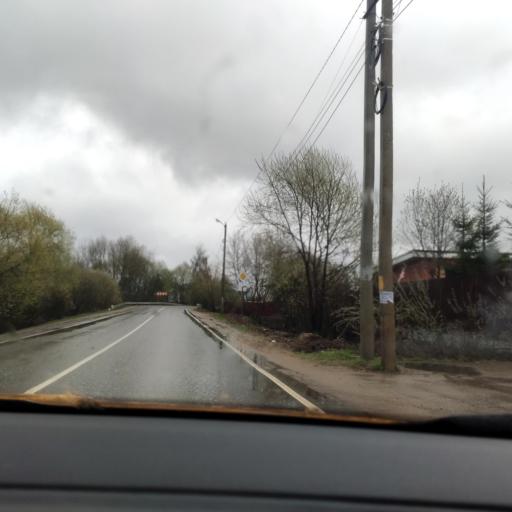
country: RU
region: Moskovskaya
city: Yershovo
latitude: 55.7521
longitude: 36.8724
